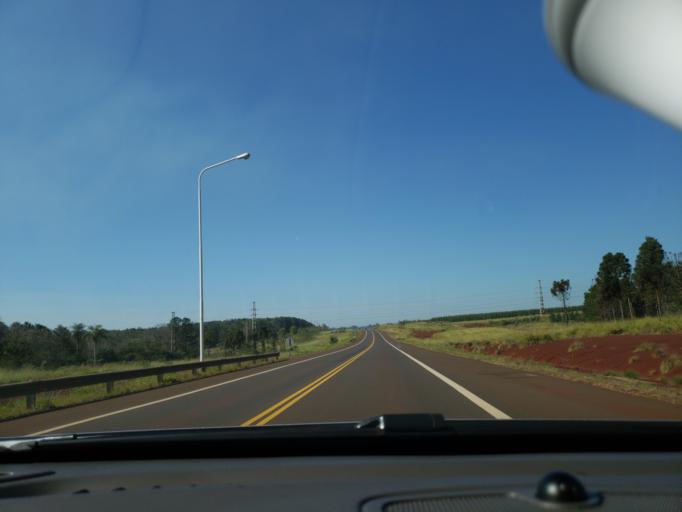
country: AR
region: Misiones
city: Garupa
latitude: -27.4656
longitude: -55.9153
